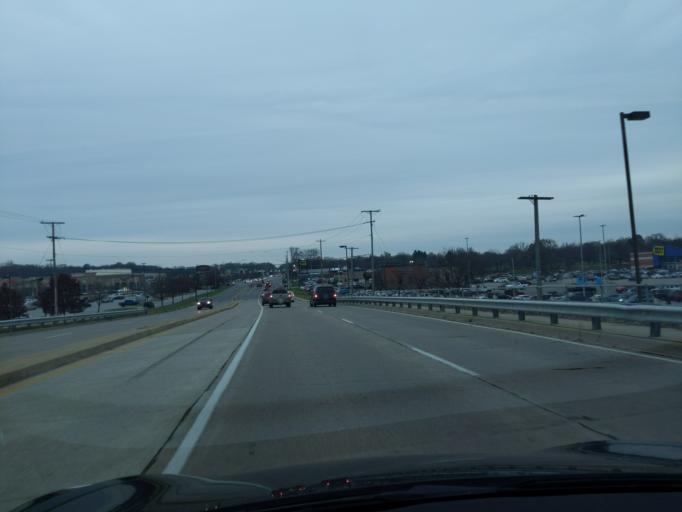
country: US
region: Indiana
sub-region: Saint Joseph County
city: Georgetown
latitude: 41.7169
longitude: -86.1876
